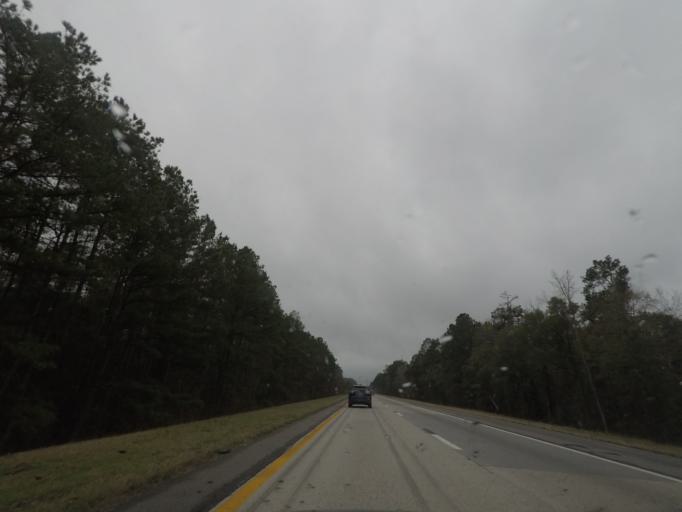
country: US
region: South Carolina
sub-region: Dorchester County
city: Saint George
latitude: 33.1076
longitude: -80.6444
